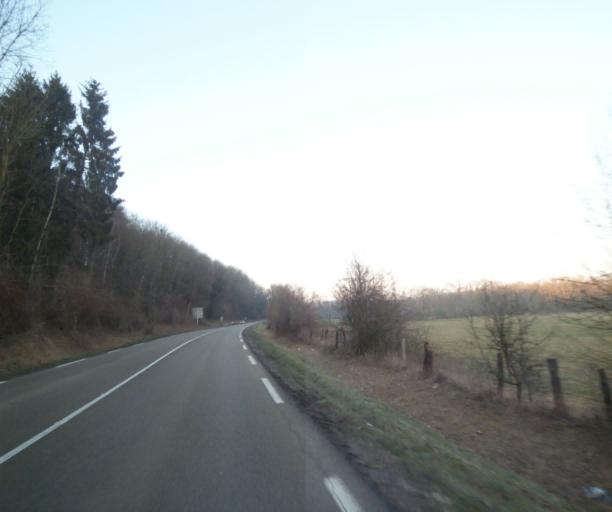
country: FR
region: Champagne-Ardenne
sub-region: Departement de la Haute-Marne
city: Bienville
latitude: 48.5967
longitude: 5.0312
